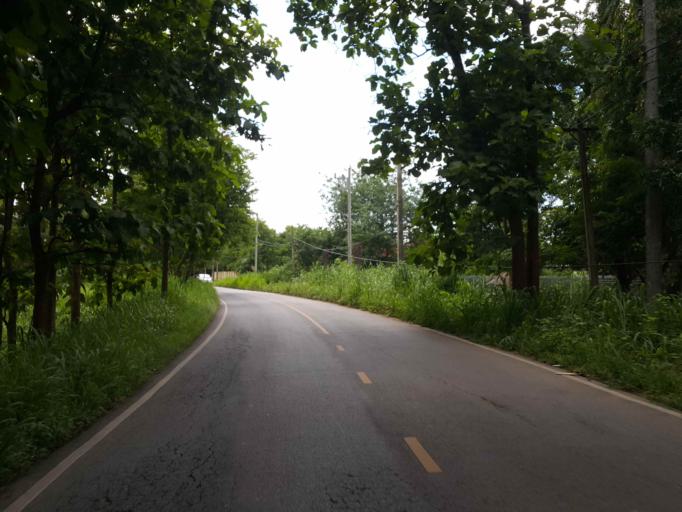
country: TH
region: Chiang Mai
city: San Sai
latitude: 18.9113
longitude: 98.9419
